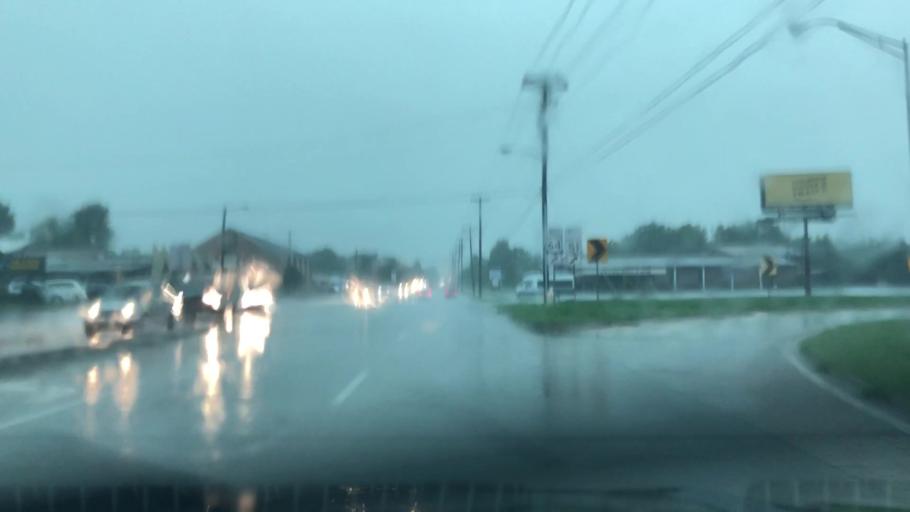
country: US
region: Oklahoma
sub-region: Tulsa County
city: Tulsa
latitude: 36.1198
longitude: -95.9223
